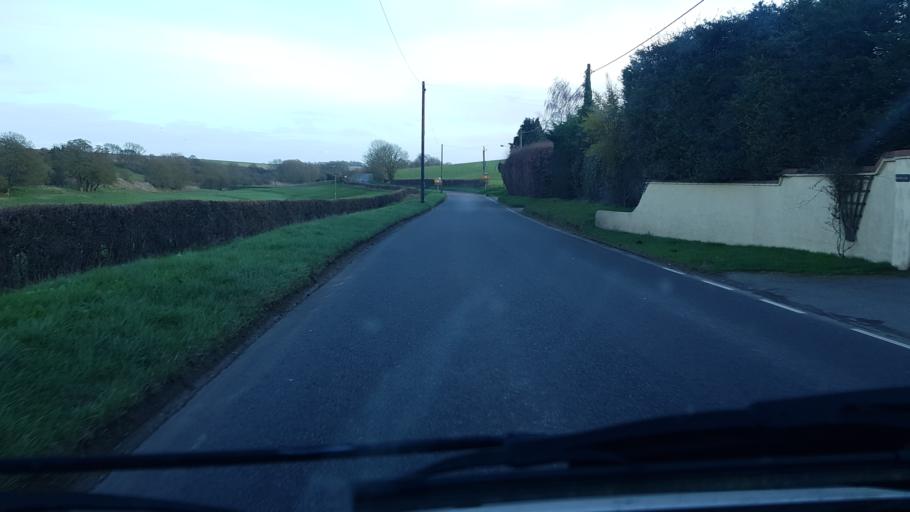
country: GB
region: England
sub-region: Wiltshire
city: Collingbourne Kingston
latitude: 51.2970
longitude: -1.6580
